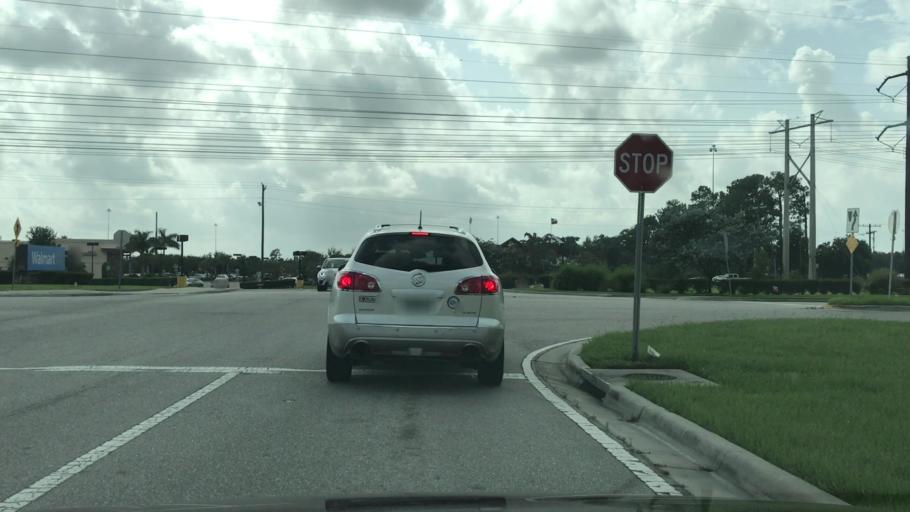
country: US
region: Florida
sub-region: Sarasota County
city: Desoto Lakes
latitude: 27.4382
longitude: -82.4536
